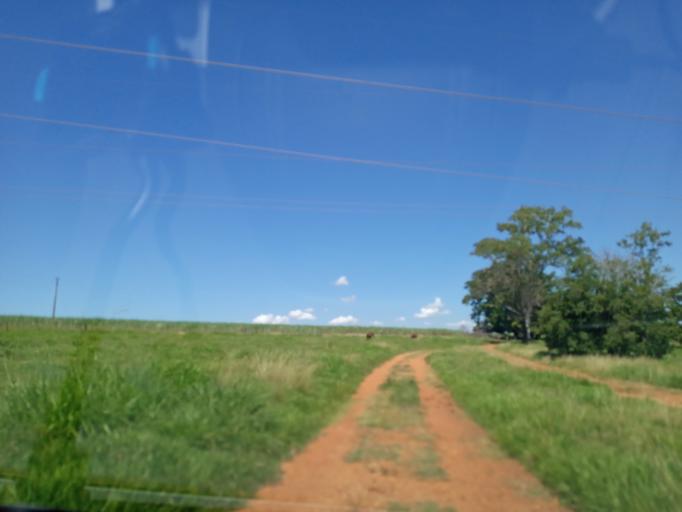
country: BR
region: Goias
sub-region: Itumbiara
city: Itumbiara
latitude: -18.3983
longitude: -49.1261
